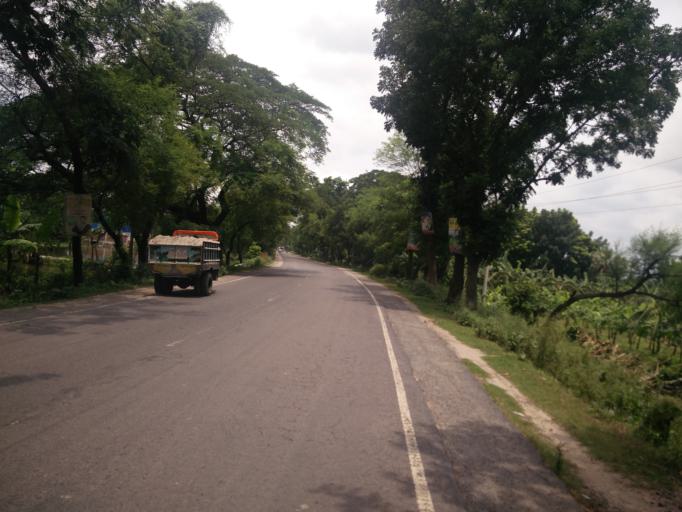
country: BD
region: Khulna
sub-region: Magura
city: Magura
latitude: 23.5440
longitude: 89.5330
